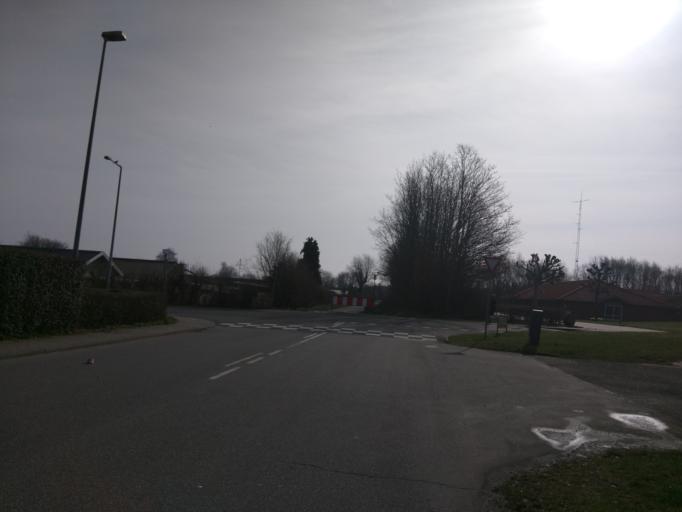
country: DK
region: South Denmark
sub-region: Fredericia Kommune
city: Snoghoj
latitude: 55.5449
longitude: 9.7034
